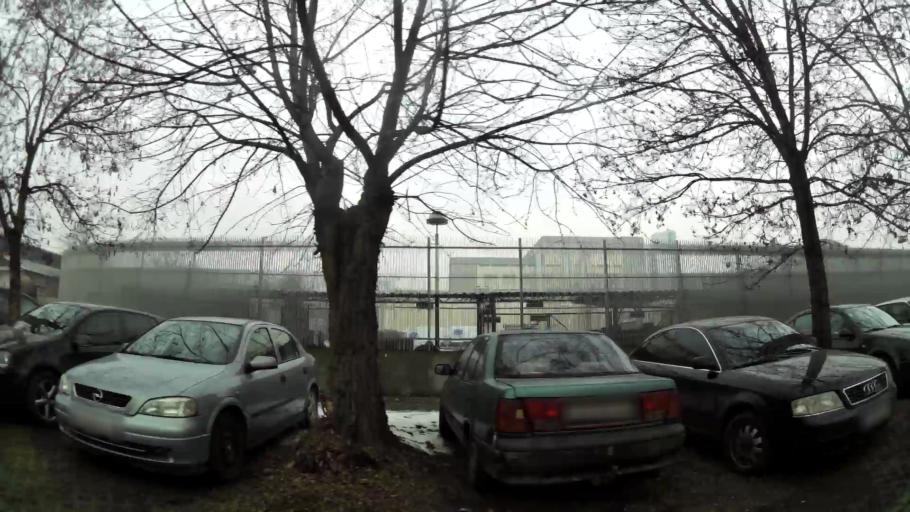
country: MK
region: Cair
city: Cair
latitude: 41.9994
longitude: 21.4657
